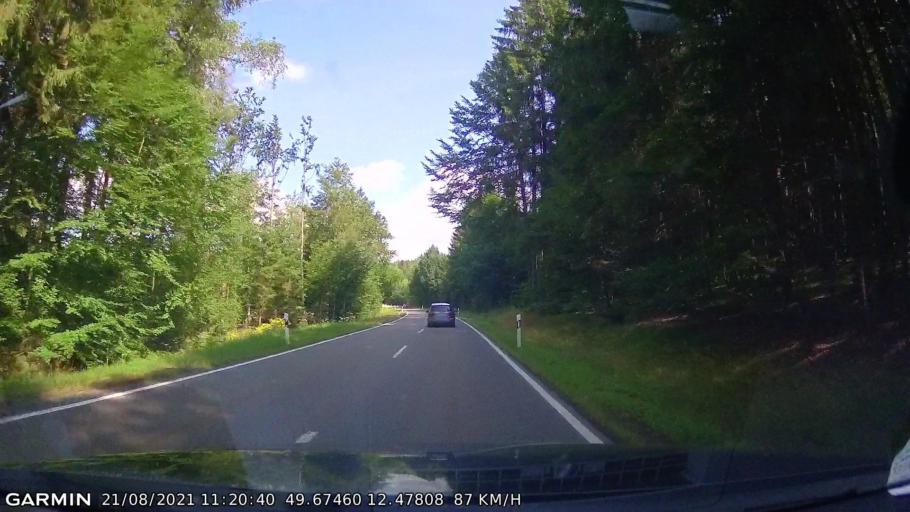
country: DE
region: Bavaria
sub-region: Upper Palatinate
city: Waidhaus
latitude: 49.6747
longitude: 12.4781
